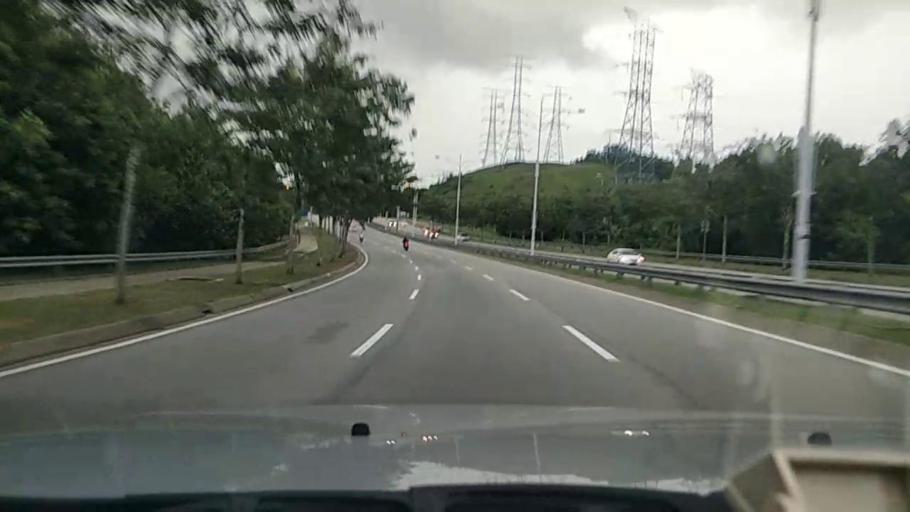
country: MY
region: Putrajaya
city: Putrajaya
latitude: 2.9532
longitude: 101.7145
